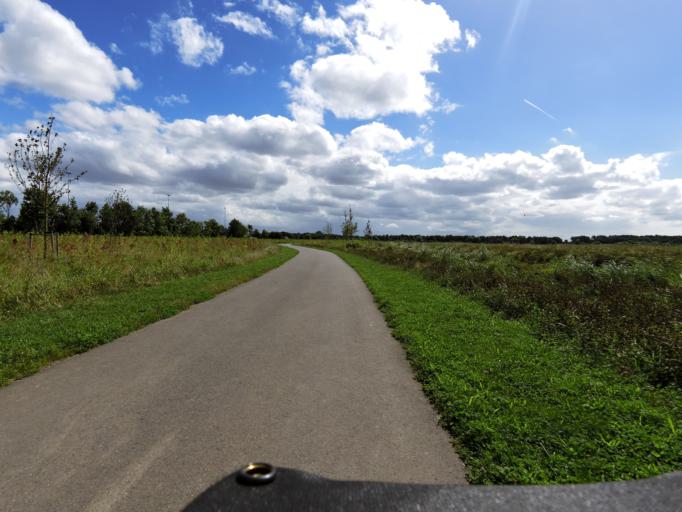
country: NL
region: South Holland
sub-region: Gemeente Zwijndrecht
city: Heerjansdam
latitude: 51.8428
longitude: 4.5512
